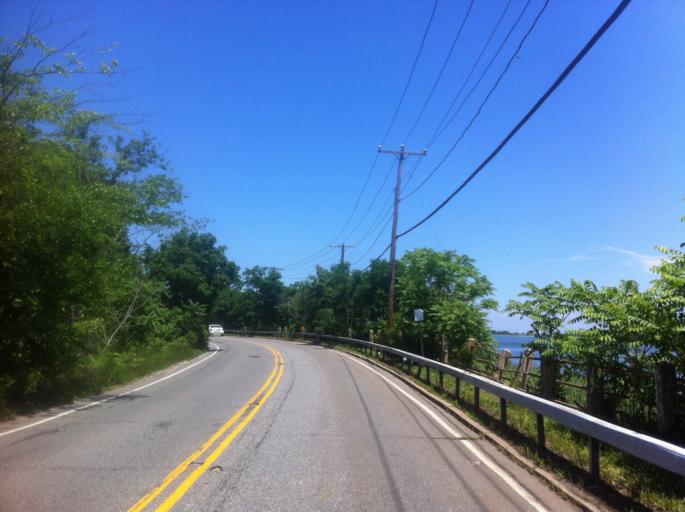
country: US
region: New York
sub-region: Nassau County
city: Bayville
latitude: 40.8887
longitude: -73.5478
